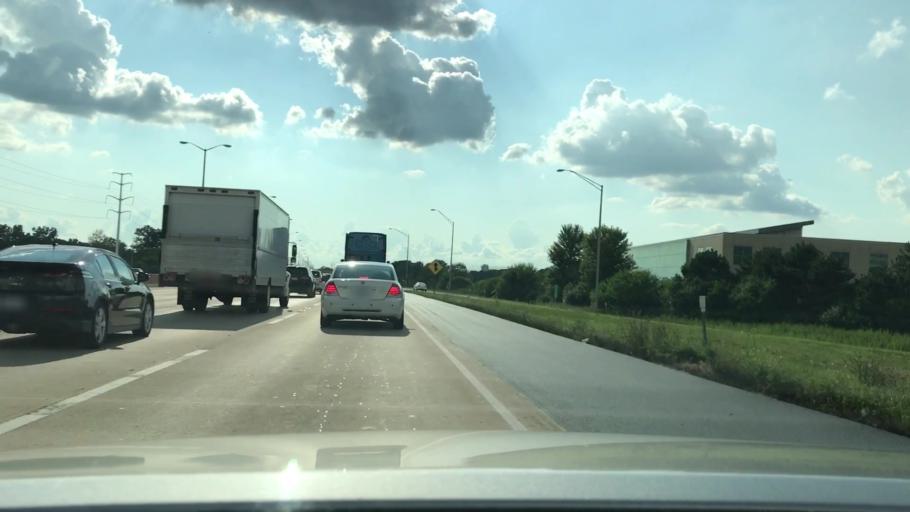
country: US
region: Illinois
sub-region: DuPage County
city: Warrenville
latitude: 41.8069
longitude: -88.1699
